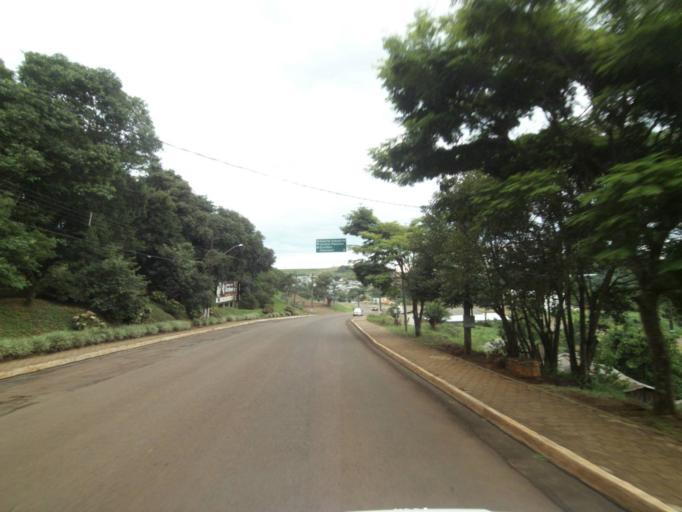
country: BR
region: Parana
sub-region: Guaraniacu
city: Guaraniacu
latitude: -25.1076
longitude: -52.8567
